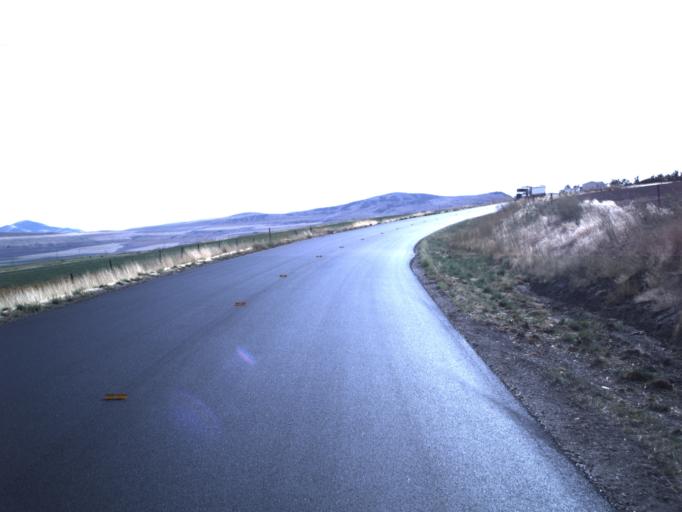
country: US
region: Utah
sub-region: Cache County
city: Benson
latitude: 41.8637
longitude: -111.9577
